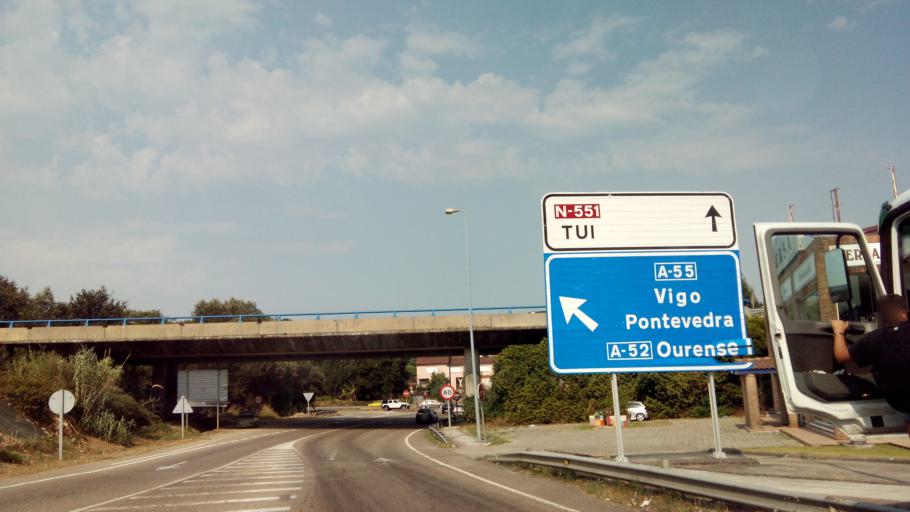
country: PT
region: Viana do Castelo
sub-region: Valenca
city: Valenca
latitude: 42.0371
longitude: -8.6583
